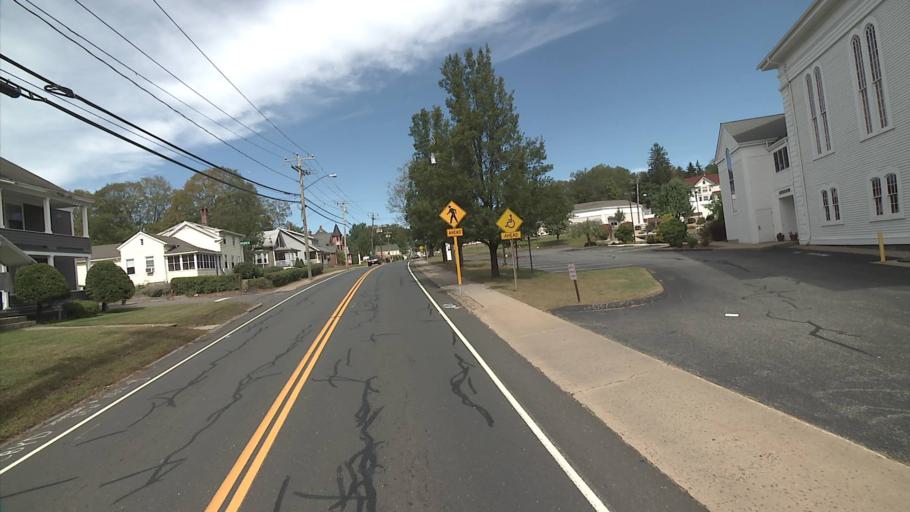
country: US
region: Connecticut
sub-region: Tolland County
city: Stafford Springs
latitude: 41.9536
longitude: -72.3086
